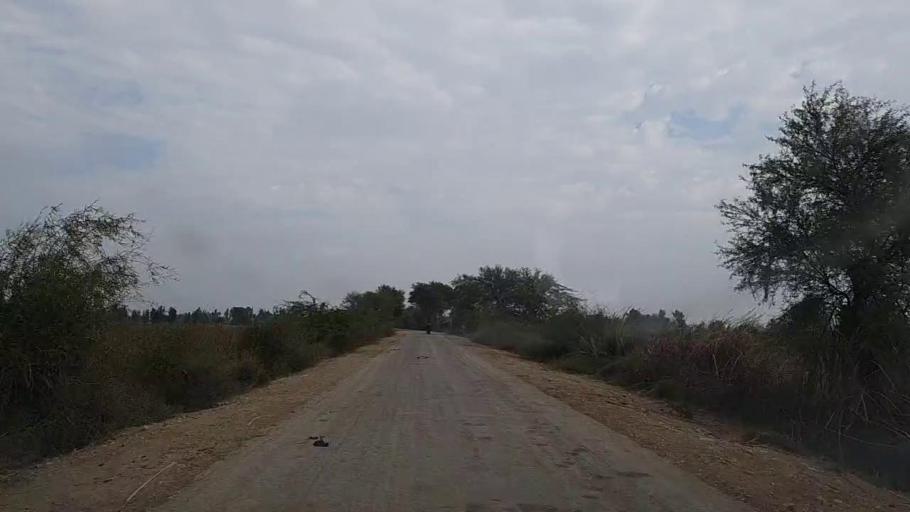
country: PK
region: Sindh
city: Sanghar
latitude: 26.2284
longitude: 69.0121
